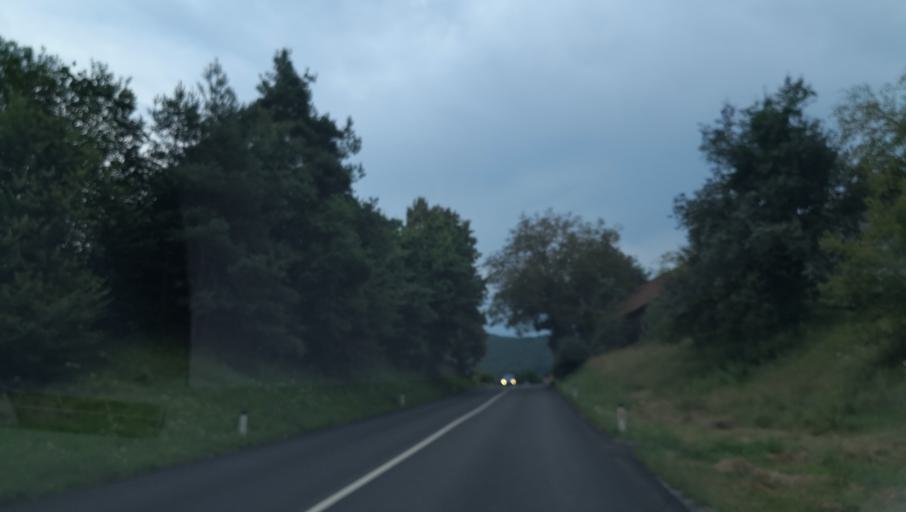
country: SI
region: Ivancna Gorica
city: Ivancna Gorica
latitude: 45.8802
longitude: 14.7991
